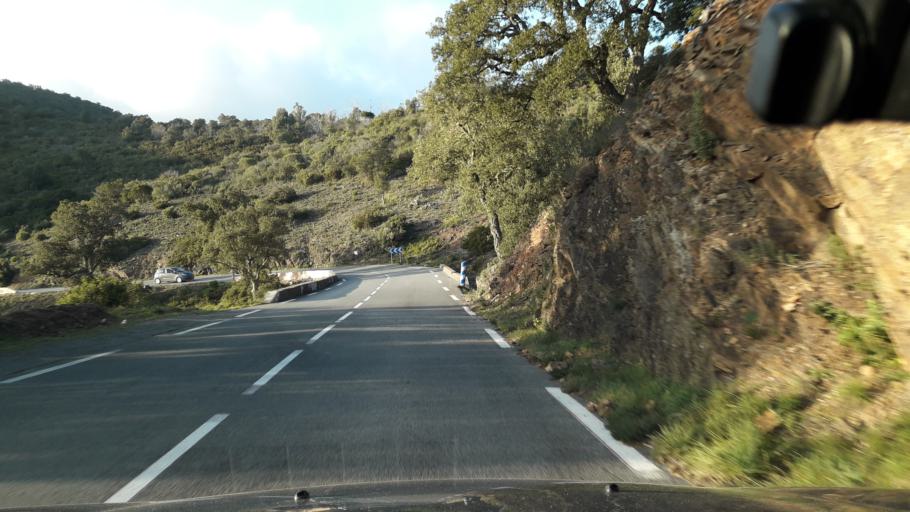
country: FR
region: Provence-Alpes-Cote d'Azur
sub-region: Departement du Var
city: Saint-Raphael
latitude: 43.5020
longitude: 6.7878
